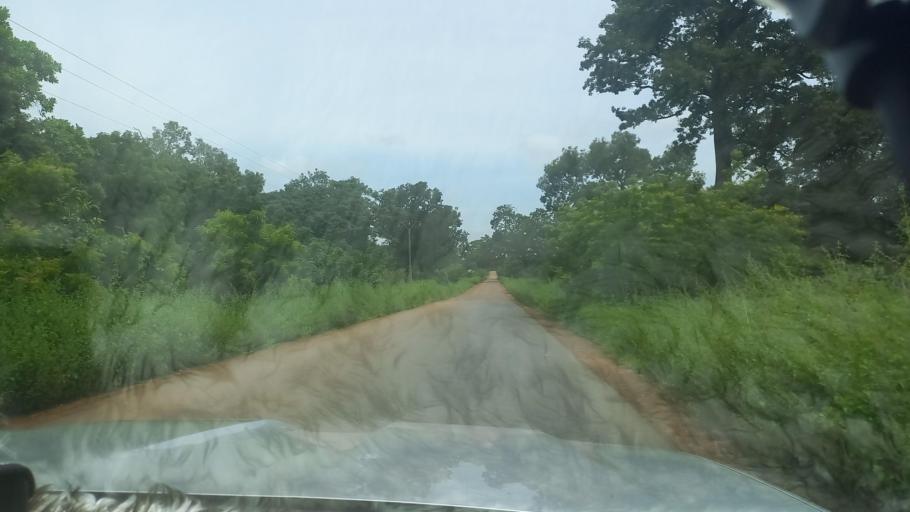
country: SN
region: Kolda
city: Marsassoum
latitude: 12.9650
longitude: -15.9699
